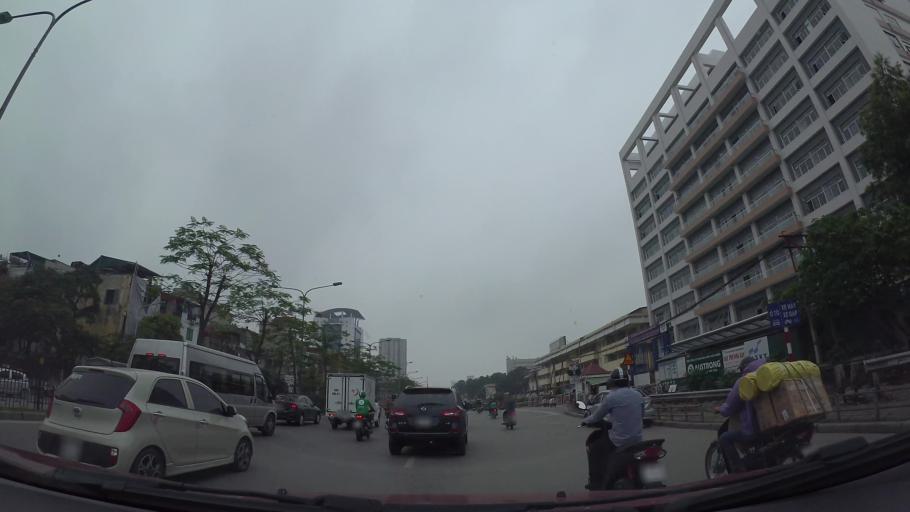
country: VN
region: Ha Noi
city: Hai BaTrung
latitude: 21.0038
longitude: 105.8413
